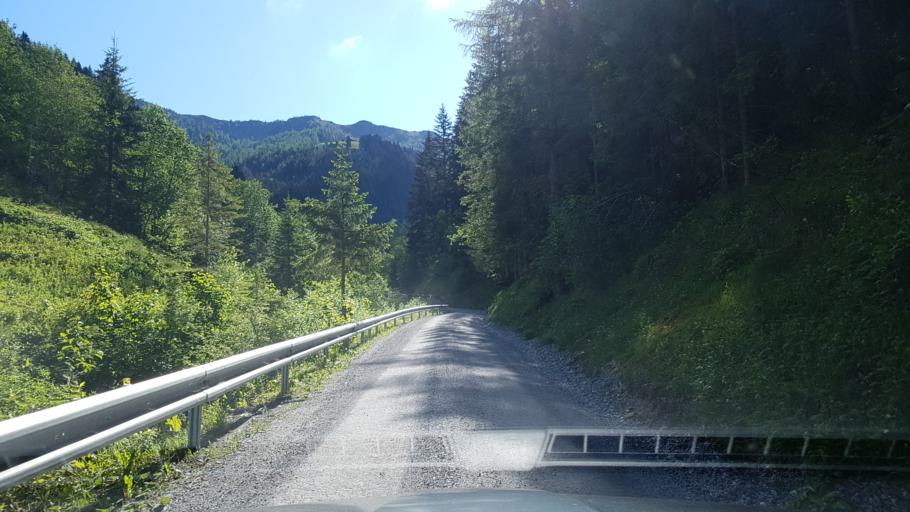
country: AT
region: Salzburg
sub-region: Politischer Bezirk Sankt Johann im Pongau
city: Kleinarl
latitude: 47.2354
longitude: 13.2595
